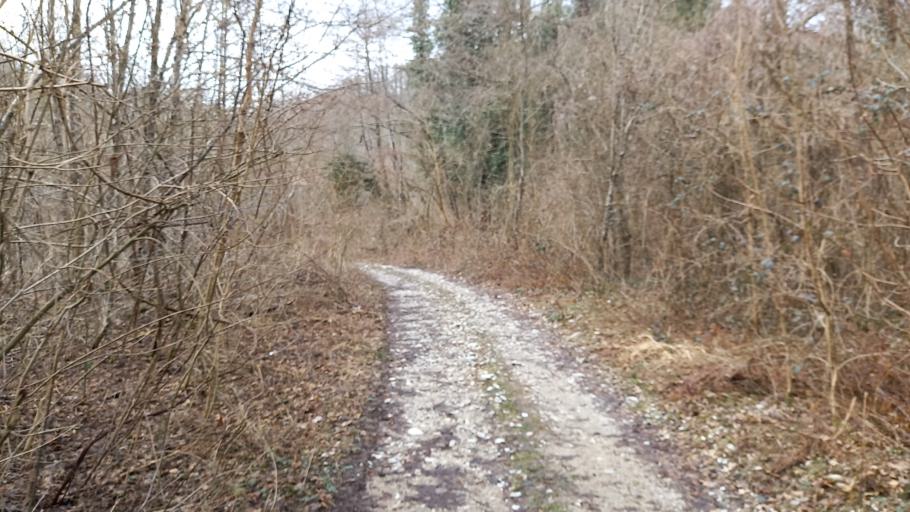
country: RU
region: Krasnodarskiy
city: Dzhubga
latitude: 44.4093
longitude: 38.7162
